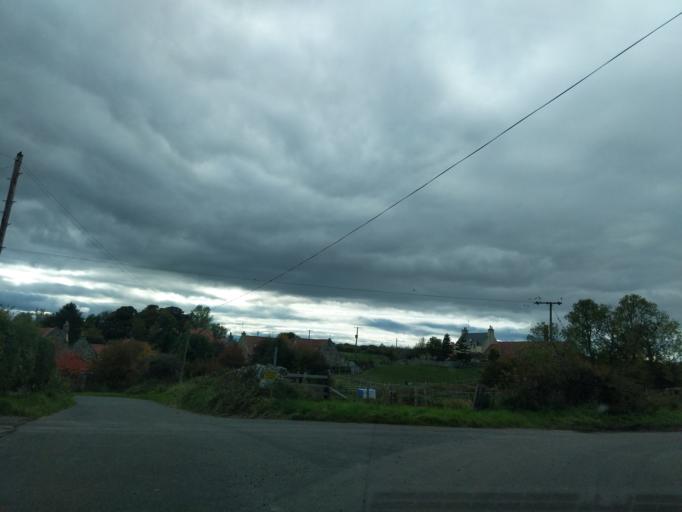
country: GB
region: Scotland
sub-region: East Lothian
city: Haddington
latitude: 55.9290
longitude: -2.8273
